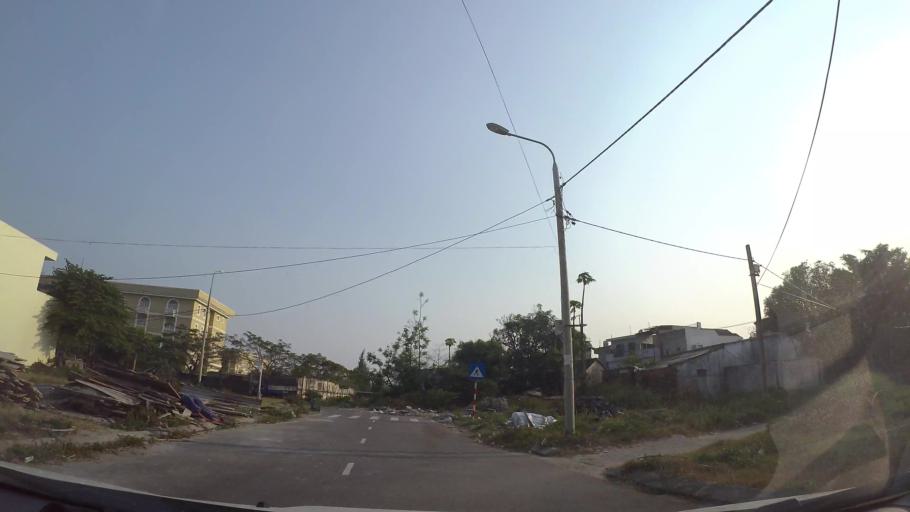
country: VN
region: Da Nang
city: Ngu Hanh Son
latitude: 15.9759
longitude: 108.2556
